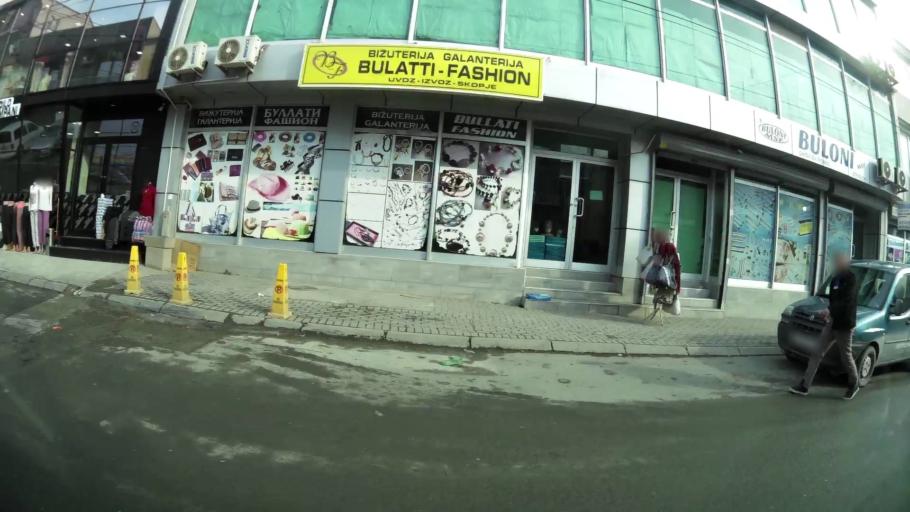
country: MK
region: Cair
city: Cair
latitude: 42.0074
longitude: 21.4344
